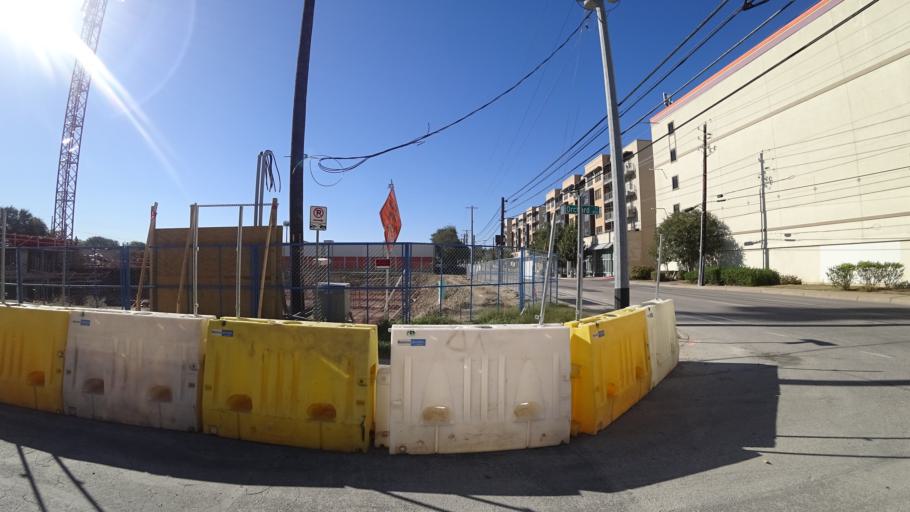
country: US
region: Texas
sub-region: Travis County
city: Austin
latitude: 30.2719
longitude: -97.7593
